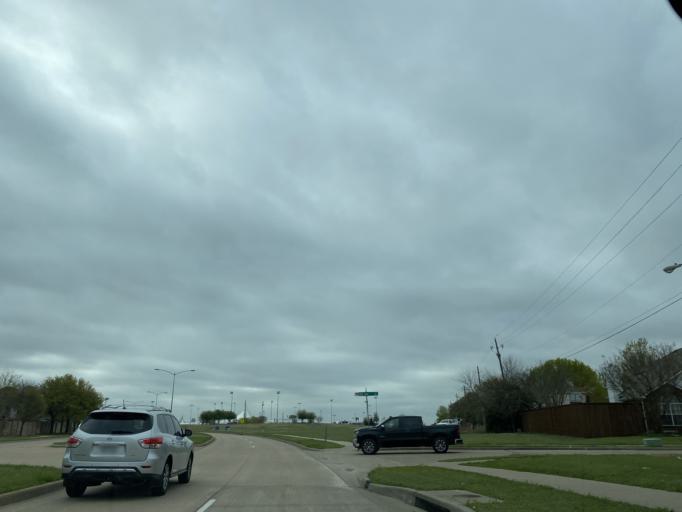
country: US
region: Texas
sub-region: Collin County
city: Allen
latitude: 33.1134
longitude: -96.6287
